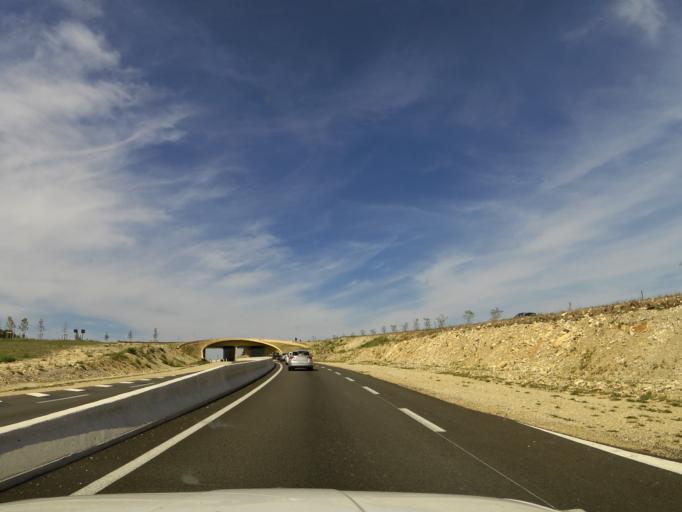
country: FR
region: Languedoc-Roussillon
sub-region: Departement du Gard
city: Nimes
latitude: 43.8556
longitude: 4.3231
